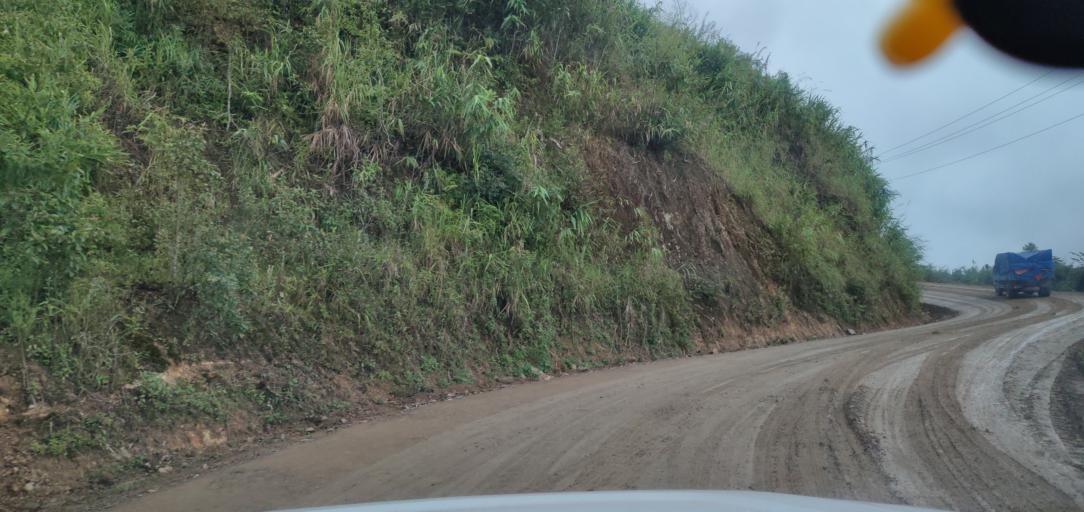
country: LA
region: Phongsali
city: Phongsali
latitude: 21.4219
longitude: 102.1752
